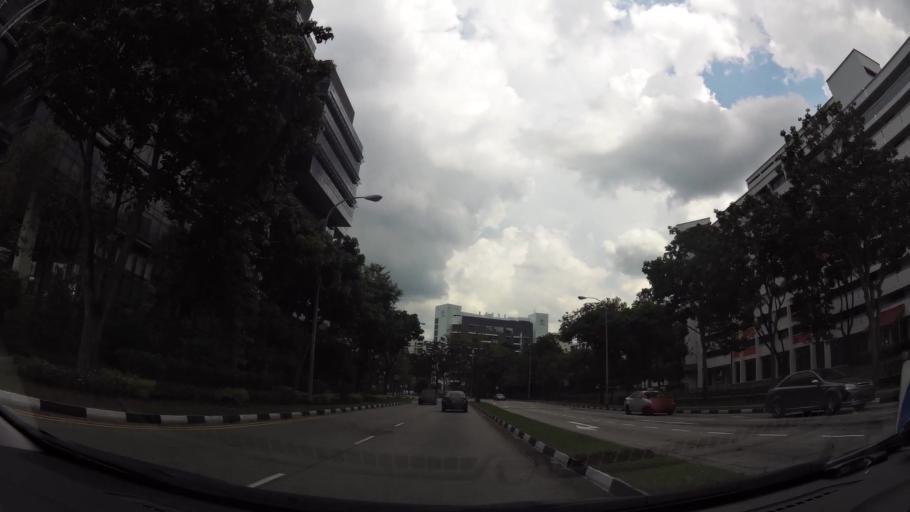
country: MY
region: Johor
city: Kampung Pasir Gudang Baru
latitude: 1.4230
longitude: 103.8369
